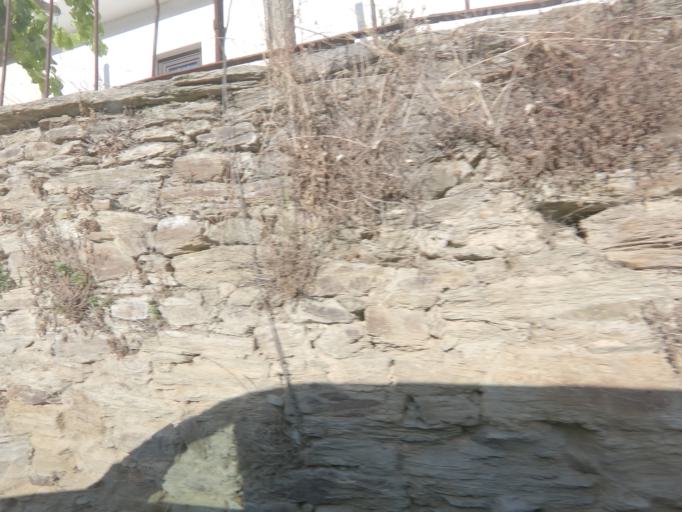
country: PT
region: Vila Real
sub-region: Sabrosa
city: Vilela
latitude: 41.1797
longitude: -7.5799
